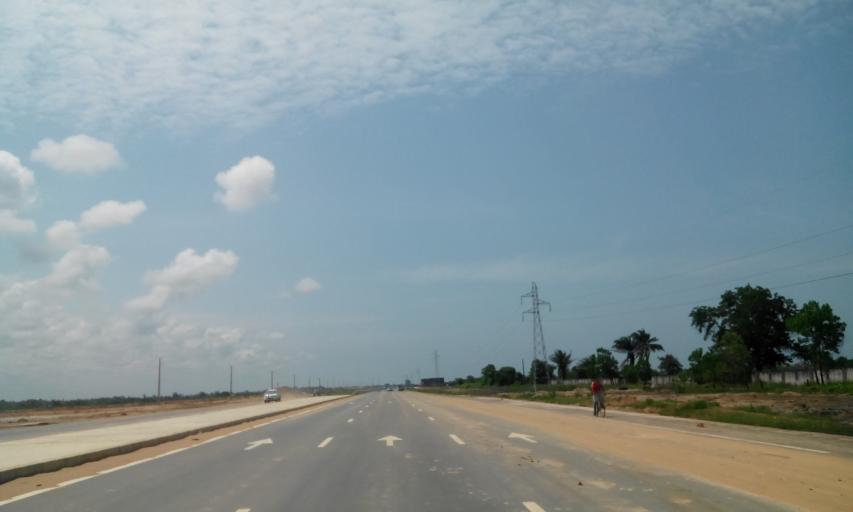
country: CI
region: Sud-Comoe
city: Grand-Bassam
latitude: 5.2311
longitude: -3.7573
